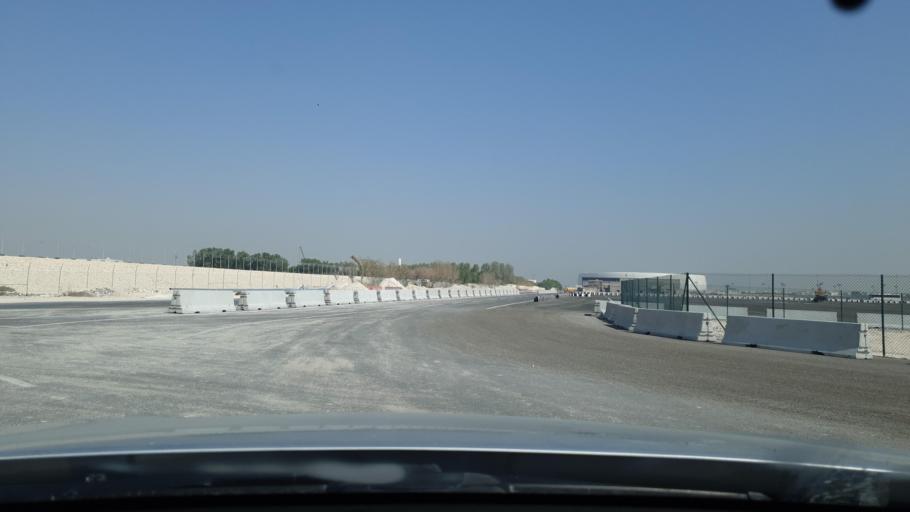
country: QA
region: Baladiyat ad Dawhah
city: Doha
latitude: 25.2232
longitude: 51.5259
